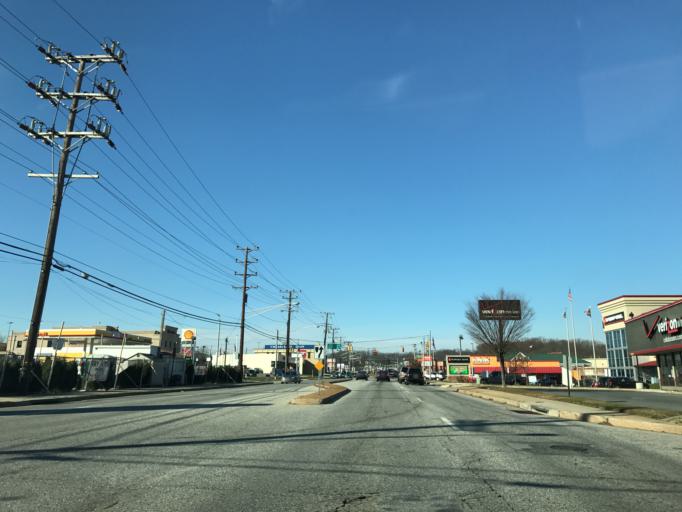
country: US
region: Maryland
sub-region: Baltimore County
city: Carney
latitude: 39.3983
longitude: -76.5413
